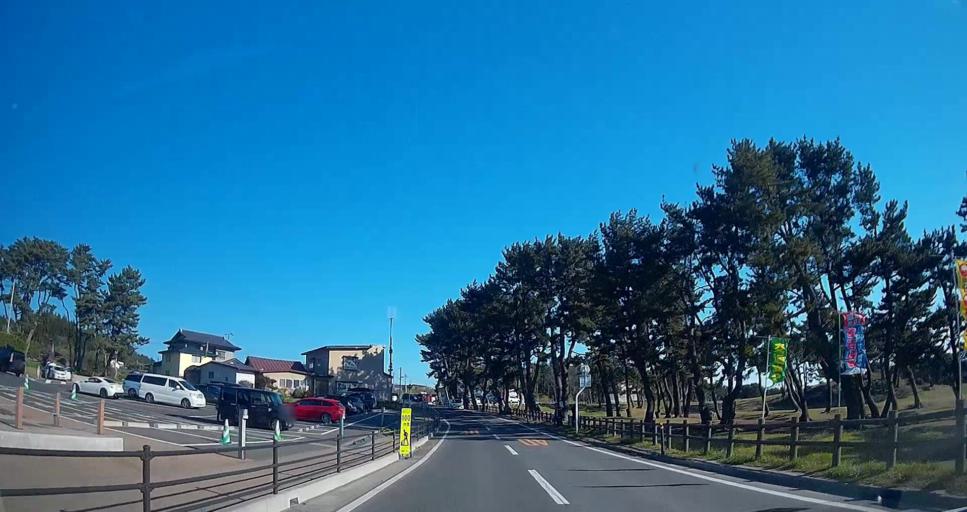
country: JP
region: Aomori
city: Hachinohe
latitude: 40.5091
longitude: 141.6085
